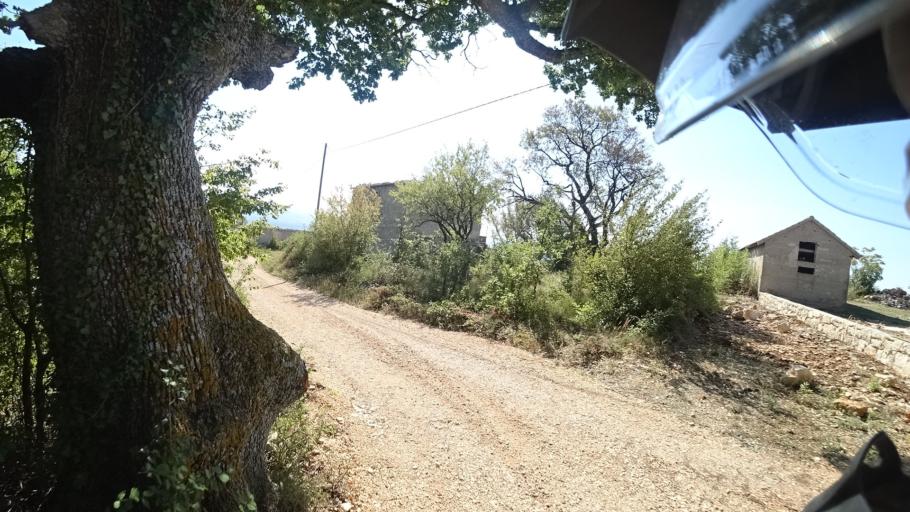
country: HR
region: Sibensko-Kniniska
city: Drnis
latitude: 43.8735
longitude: 16.1847
